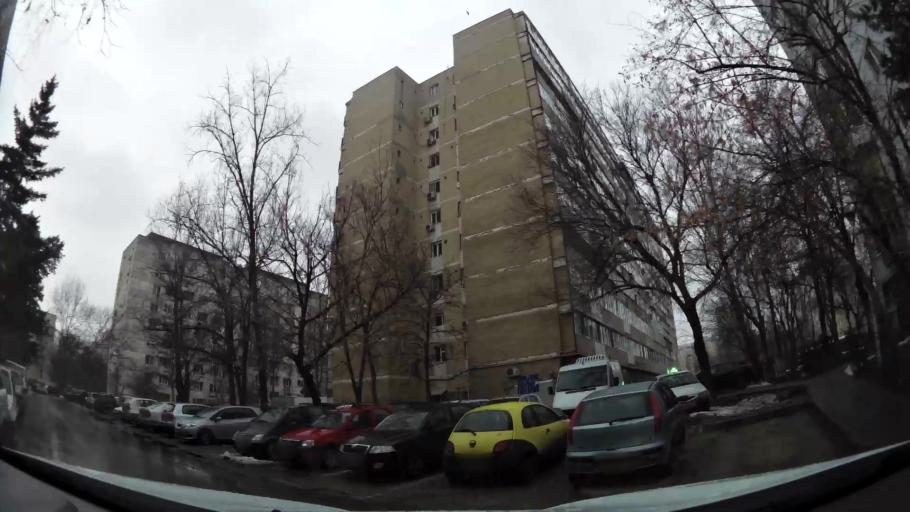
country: RO
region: Ilfov
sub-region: Comuna Chiajna
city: Rosu
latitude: 44.4160
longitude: 26.0215
